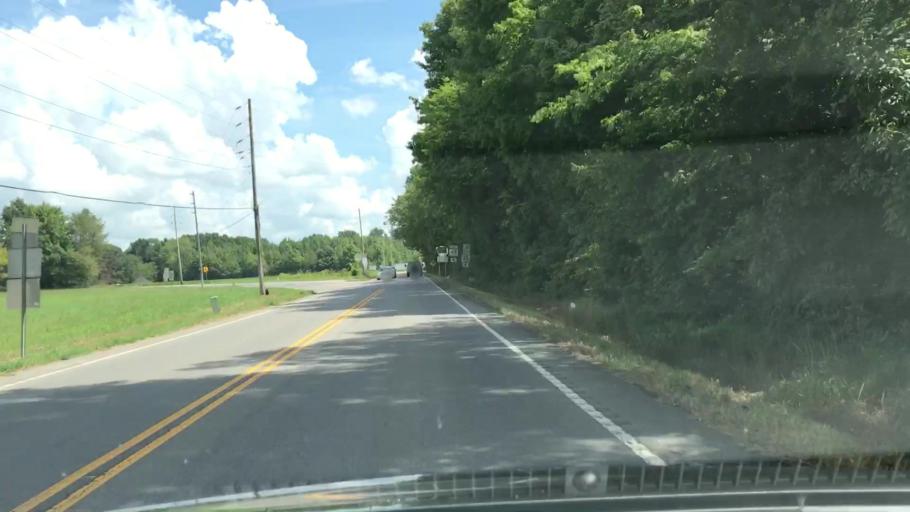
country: US
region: Tennessee
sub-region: Robertson County
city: Springfield
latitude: 36.5554
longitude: -86.8018
